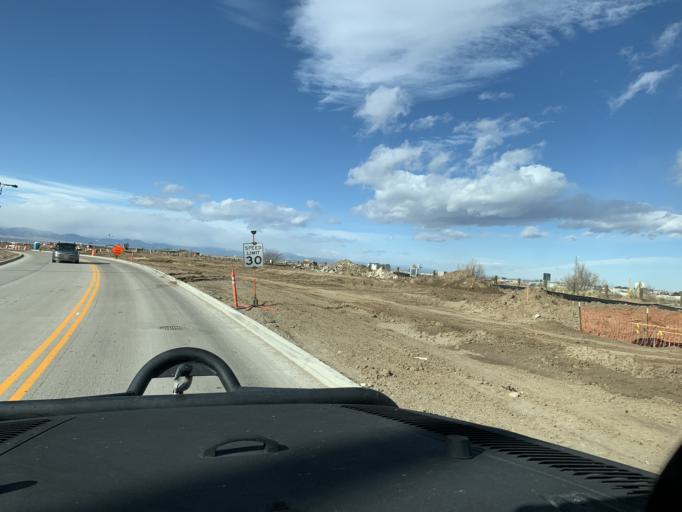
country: US
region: Colorado
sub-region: Adams County
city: Aurora
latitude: 39.7572
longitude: -104.8547
